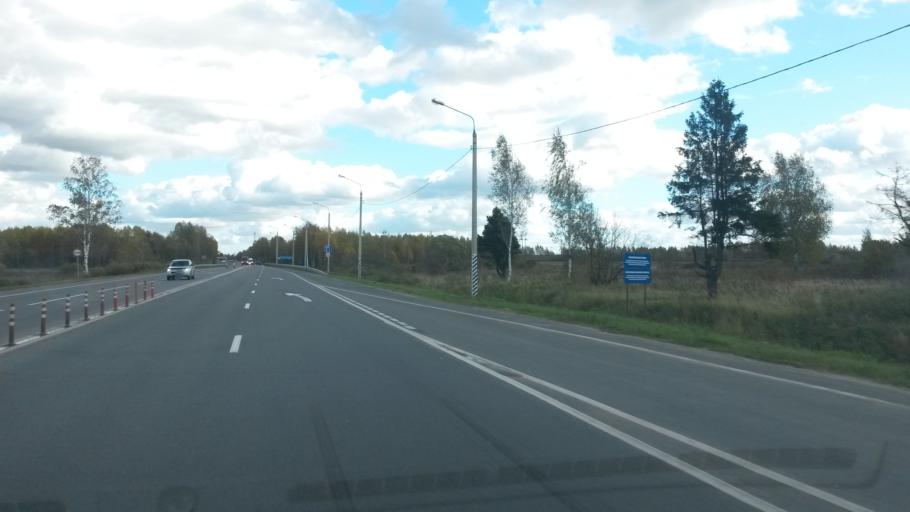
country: RU
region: Jaroslavl
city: Tunoshna
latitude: 57.5384
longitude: 40.0073
